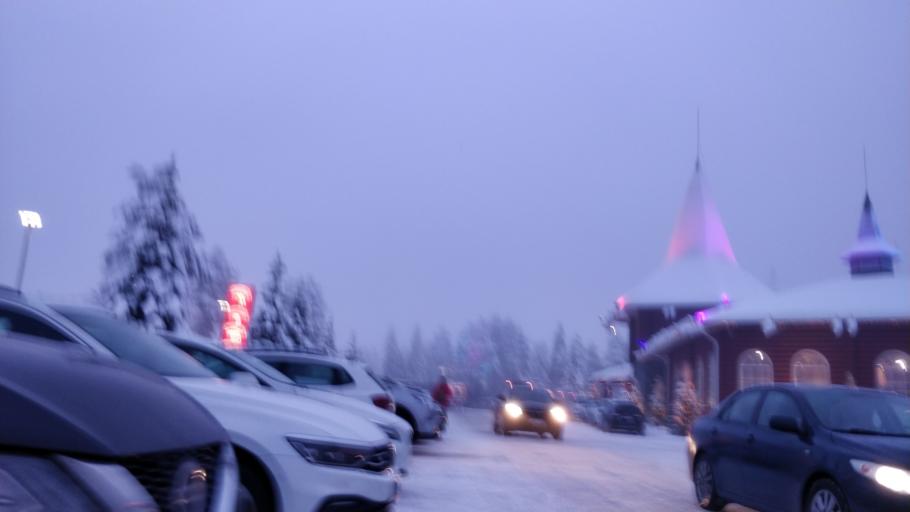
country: FI
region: Lapland
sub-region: Rovaniemi
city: Rovaniemi
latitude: 66.5433
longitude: 25.8419
